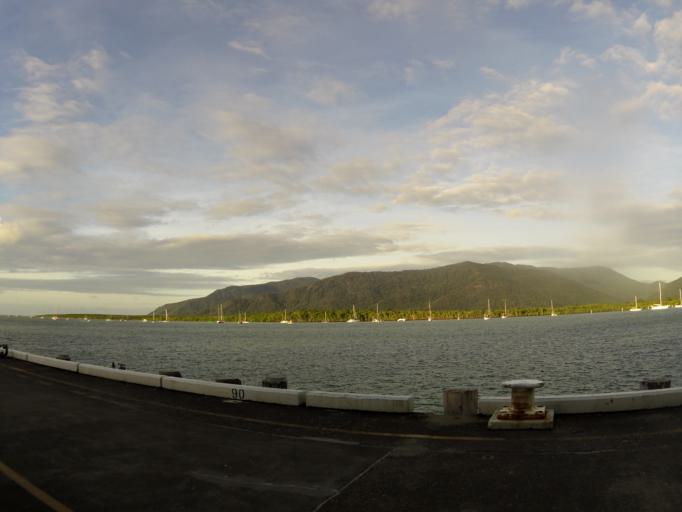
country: AU
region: Queensland
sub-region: Cairns
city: Cairns
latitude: -16.9255
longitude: 145.7806
